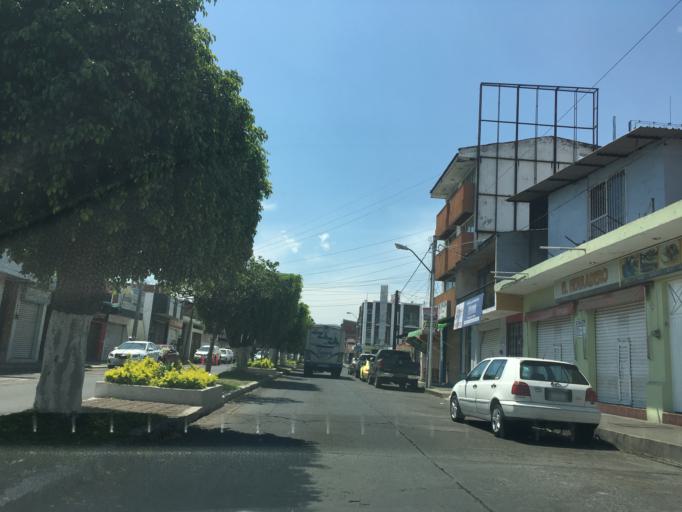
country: MX
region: Michoacan
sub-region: Uruapan
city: Uruapan
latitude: 19.4155
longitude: -102.0536
